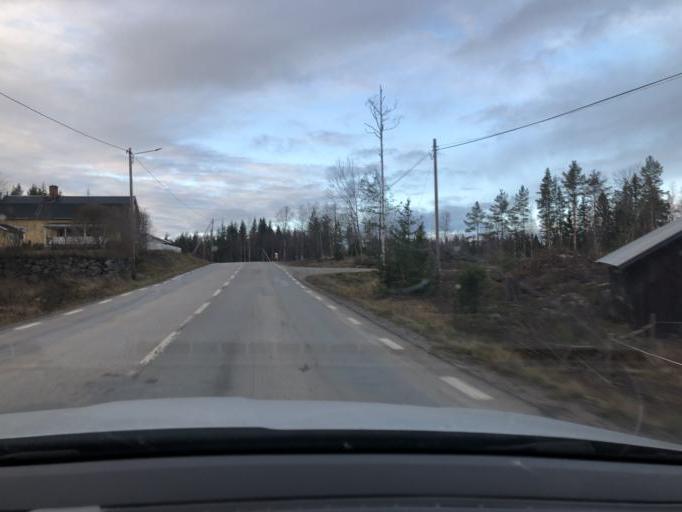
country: SE
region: Gaevleborg
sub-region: Hudiksvalls Kommun
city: Iggesund
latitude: 61.5504
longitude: 16.9928
